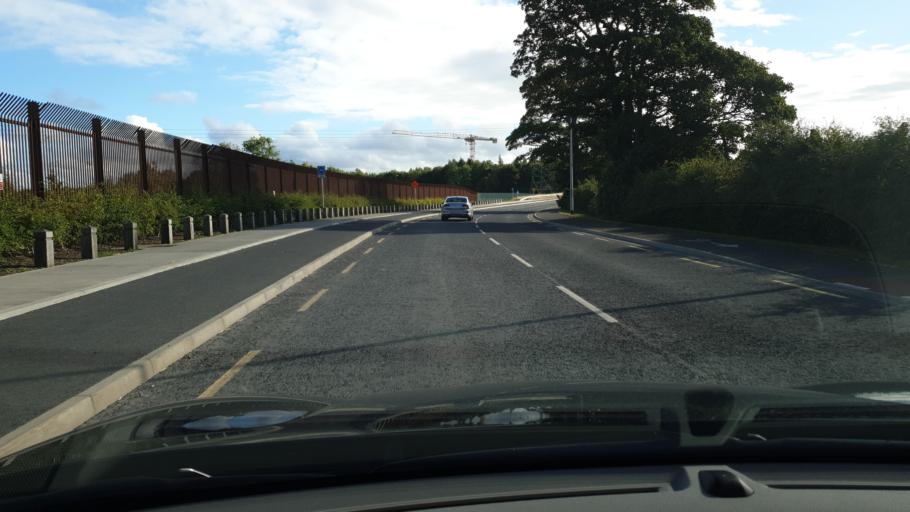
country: IE
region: Leinster
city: Hartstown
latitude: 53.4154
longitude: -6.4409
